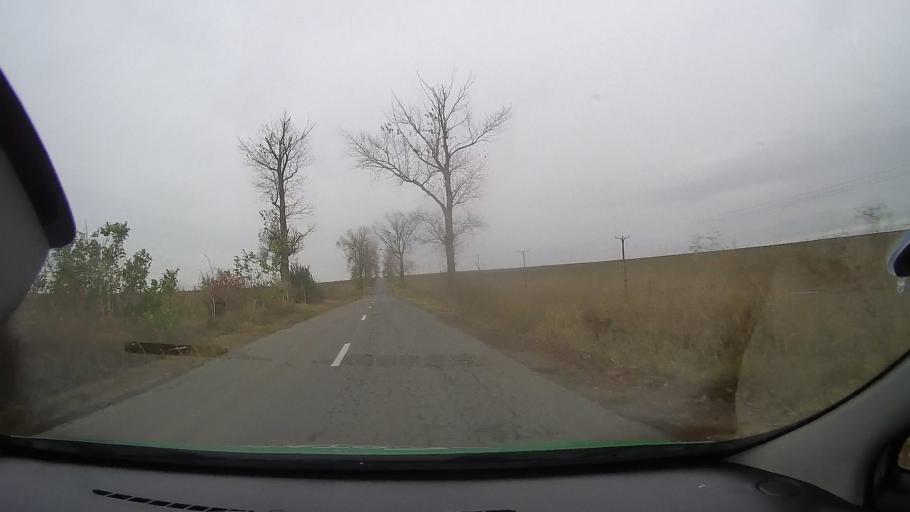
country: RO
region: Constanta
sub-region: Comuna Pantelimon
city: Pantelimon
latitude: 44.5578
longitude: 28.3237
